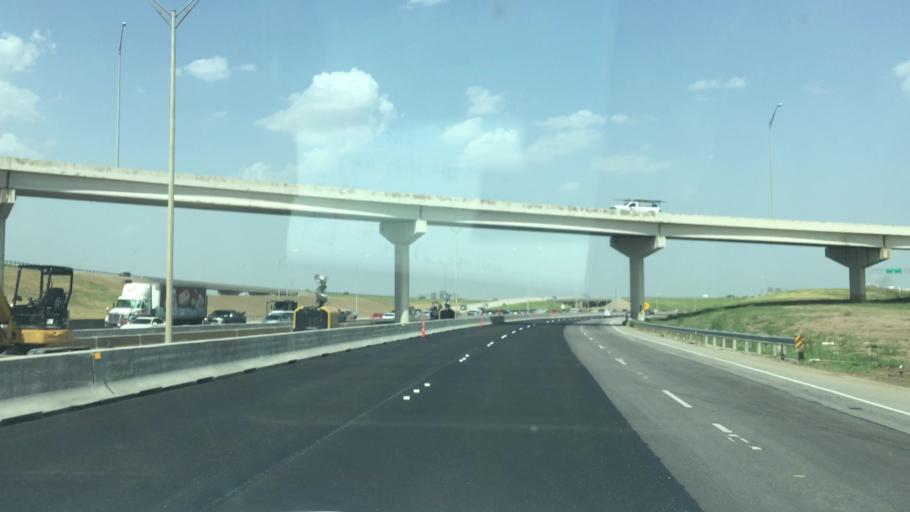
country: US
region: Texas
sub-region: Tarrant County
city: Euless
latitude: 32.8380
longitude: -97.0606
